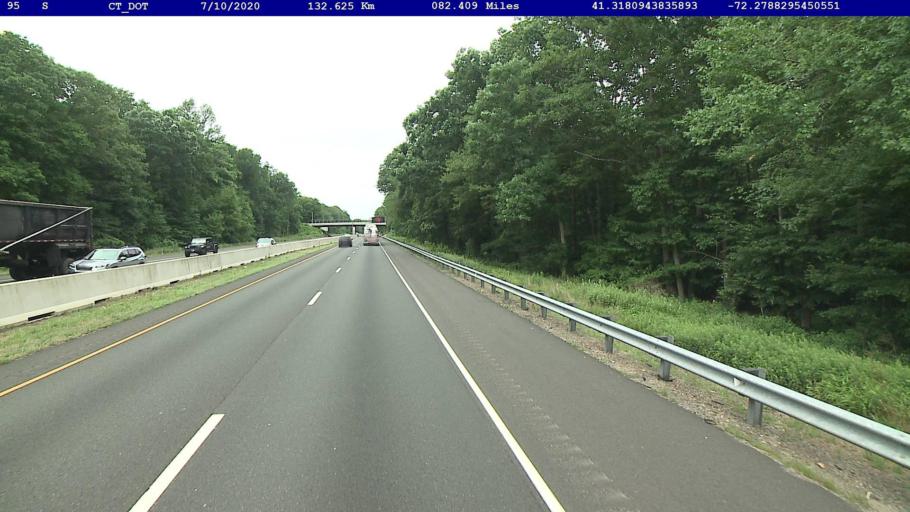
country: US
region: Connecticut
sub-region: New London County
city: Niantic
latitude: 41.3181
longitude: -72.2788
